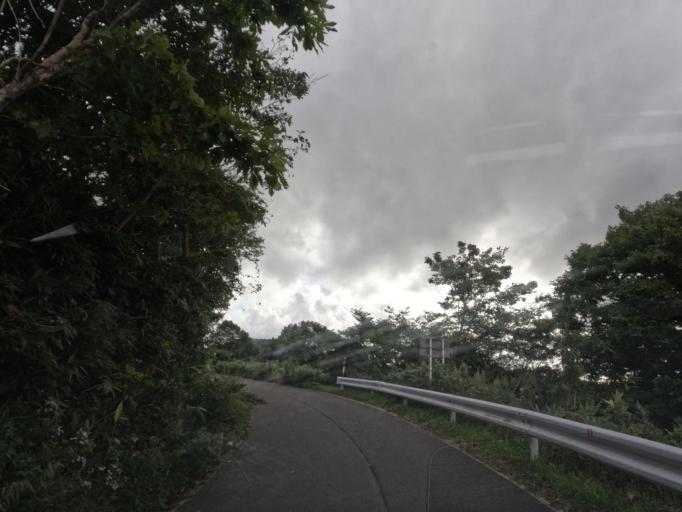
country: JP
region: Hokkaido
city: Muroran
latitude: 42.3208
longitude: 141.0030
